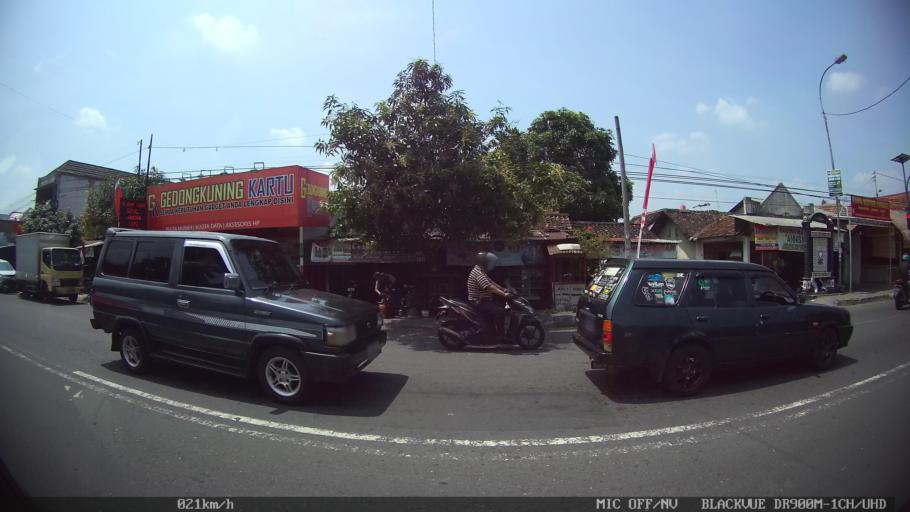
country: ID
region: Daerah Istimewa Yogyakarta
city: Yogyakarta
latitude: -7.8199
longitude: 110.4007
